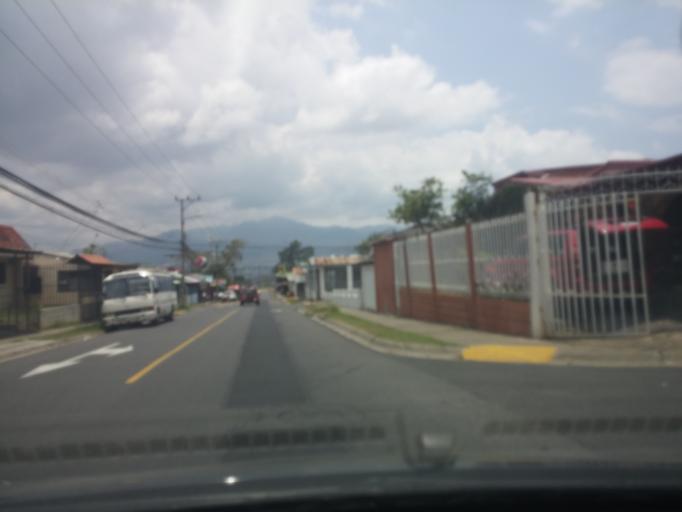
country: CR
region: Heredia
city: Llorente
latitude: 9.9878
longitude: -84.1490
